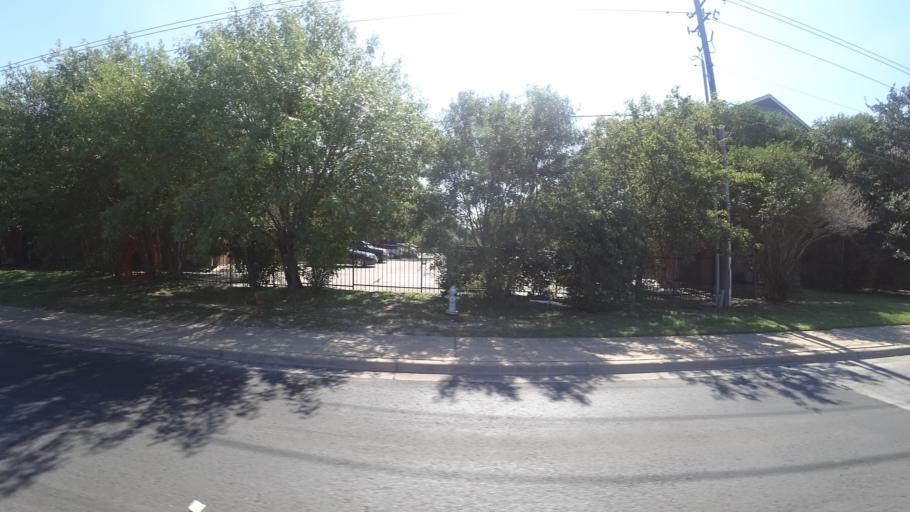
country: US
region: Texas
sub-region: Travis County
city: Austin
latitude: 30.3225
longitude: -97.6812
